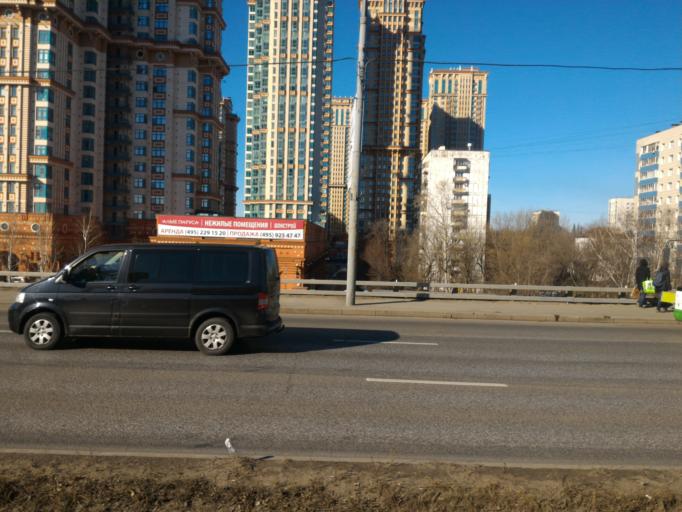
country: RU
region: Moscow
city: Shchukino
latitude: 55.8054
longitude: 37.4506
